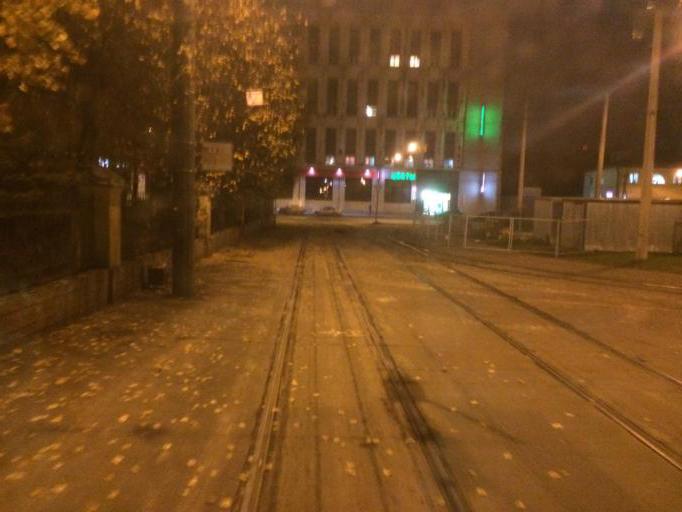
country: RU
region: St.-Petersburg
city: Obukhovo
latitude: 59.8635
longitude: 30.4732
